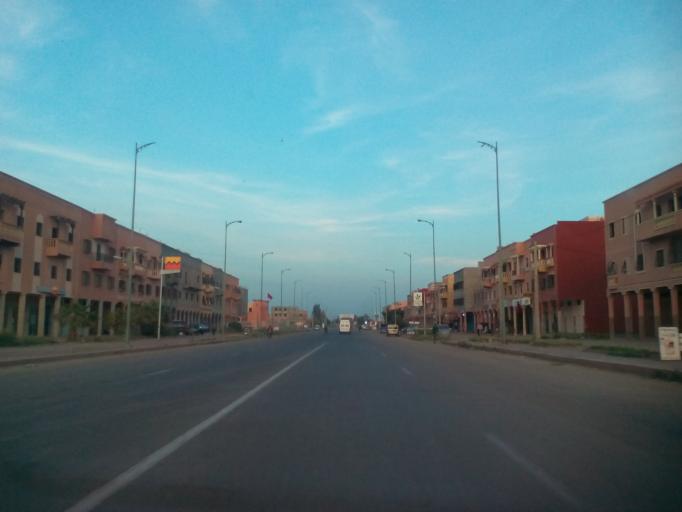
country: MA
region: Marrakech-Tensift-Al Haouz
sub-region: Marrakech
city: Marrakesh
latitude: 31.6344
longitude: -8.2455
